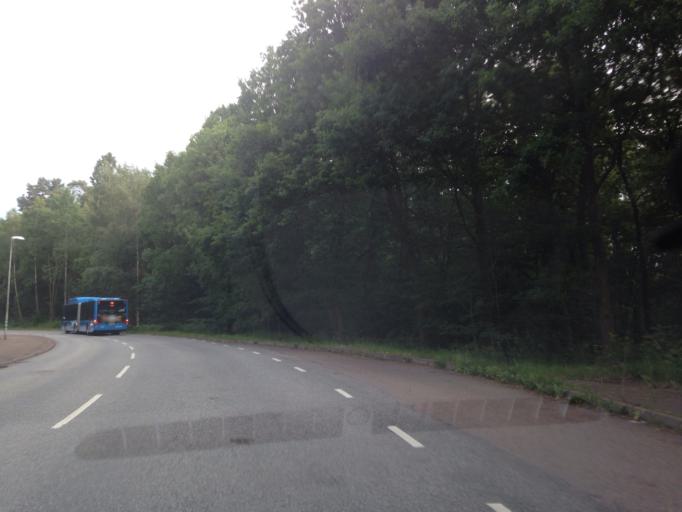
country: SE
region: Vaestra Goetaland
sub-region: Goteborg
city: Goeteborg
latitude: 57.7572
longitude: 11.9679
